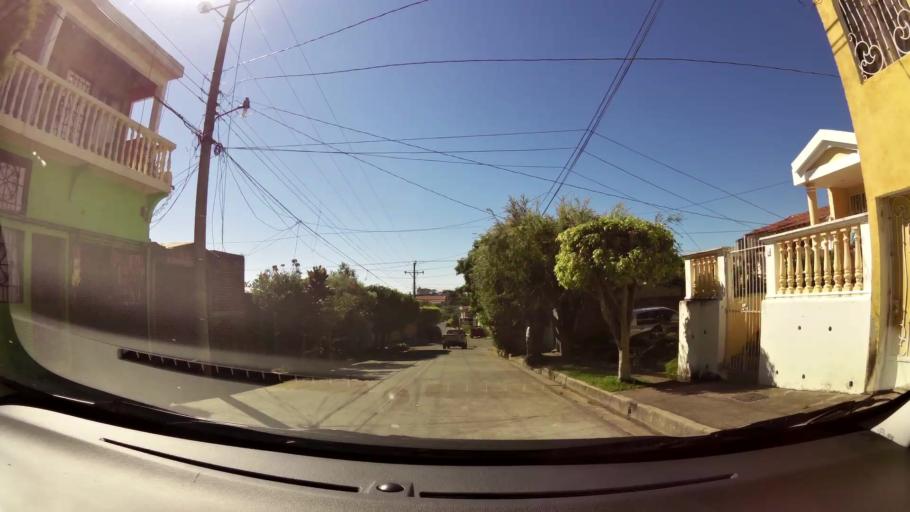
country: SV
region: Sonsonate
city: Juayua
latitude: 13.8453
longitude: -89.7438
